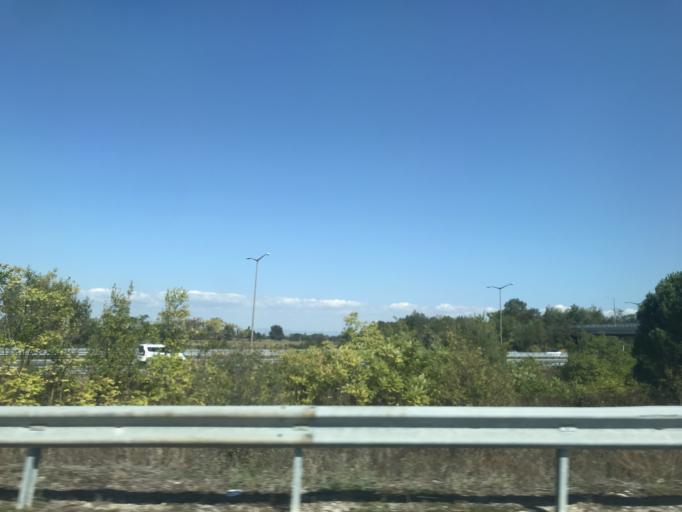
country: TR
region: Kirklareli
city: Luleburgaz
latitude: 41.4493
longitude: 27.3886
